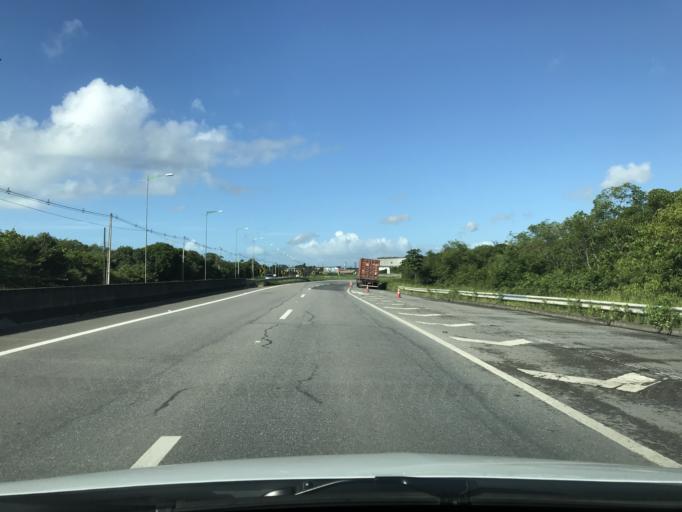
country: BR
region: Pernambuco
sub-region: Cabo De Santo Agostinho
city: Cabo
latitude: -8.3339
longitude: -35.0000
